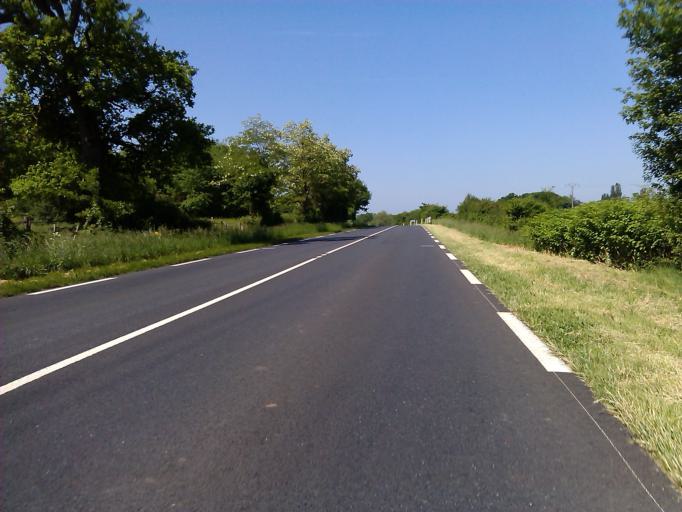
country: FR
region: Centre
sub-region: Departement de l'Indre
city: Le Pechereau
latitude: 46.5959
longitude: 1.5751
